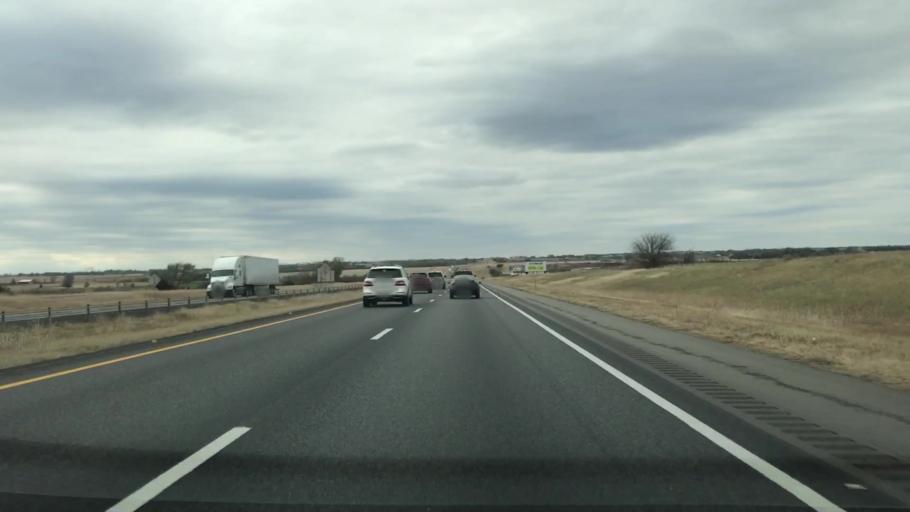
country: US
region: Oklahoma
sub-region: Beckham County
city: Elk City
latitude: 35.3858
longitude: -99.4207
